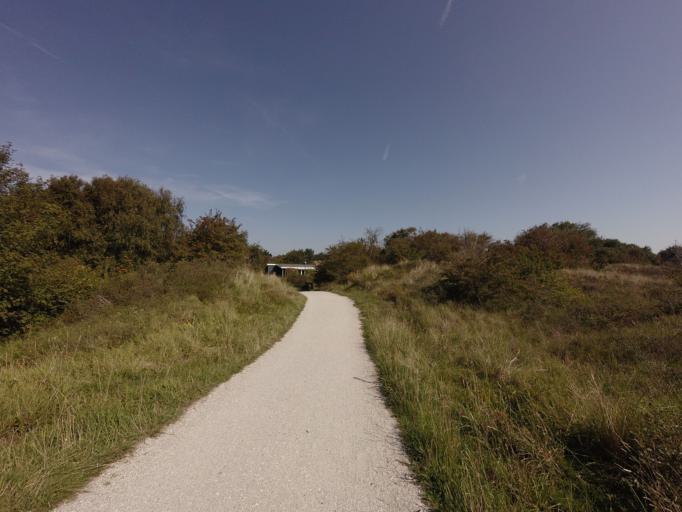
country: NL
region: Friesland
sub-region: Gemeente Schiermonnikoog
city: Schiermonnikoog
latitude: 53.4781
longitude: 6.1444
